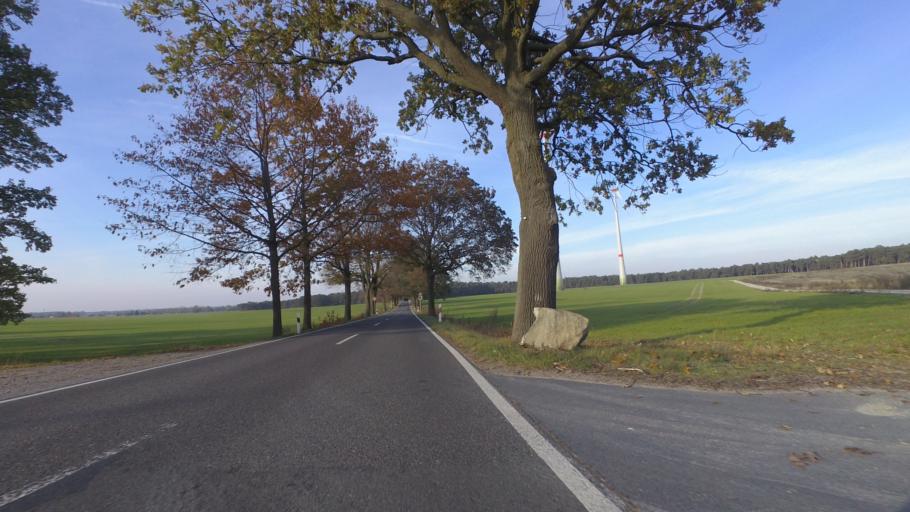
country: DE
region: Brandenburg
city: Trebbin
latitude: 52.2075
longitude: 13.3042
